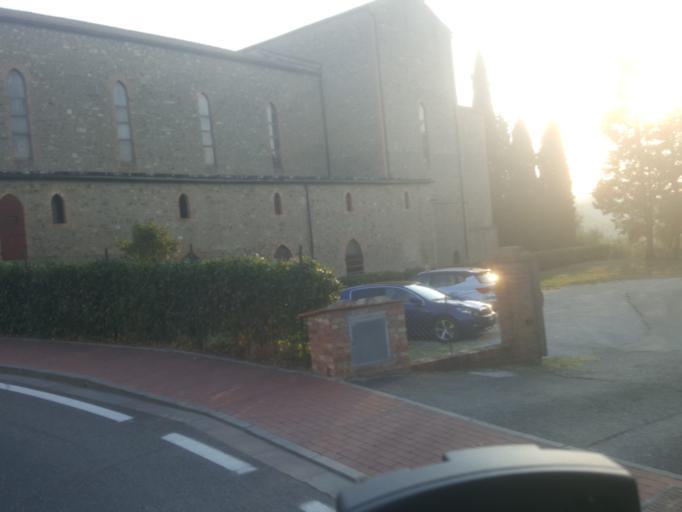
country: IT
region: Tuscany
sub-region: Province of Florence
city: Gambassi Terme
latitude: 43.5410
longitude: 10.9549
